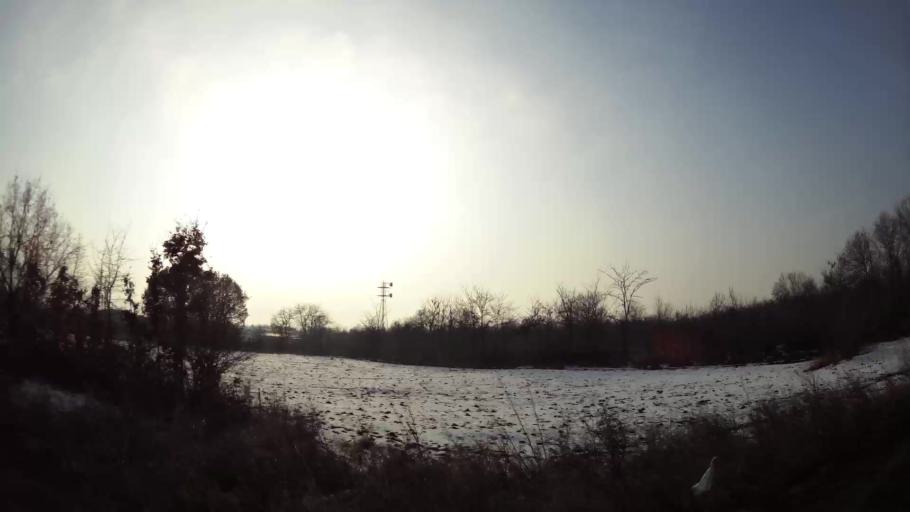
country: MK
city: Miladinovci
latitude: 41.9736
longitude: 21.6326
